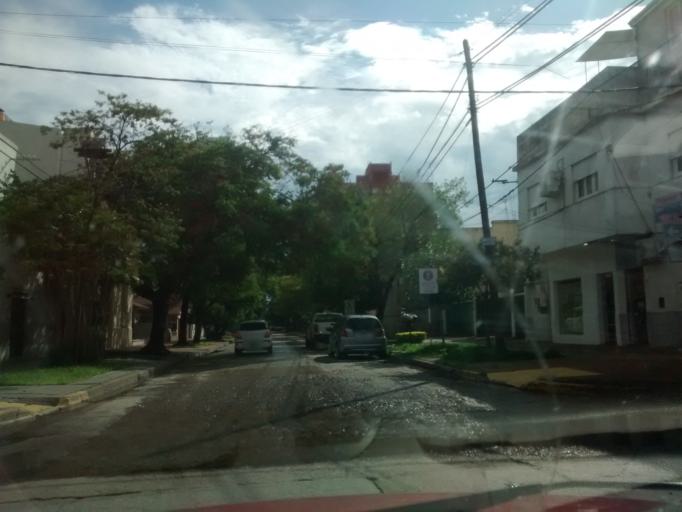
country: AR
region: Chaco
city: Resistencia
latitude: -27.4469
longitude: -58.9835
